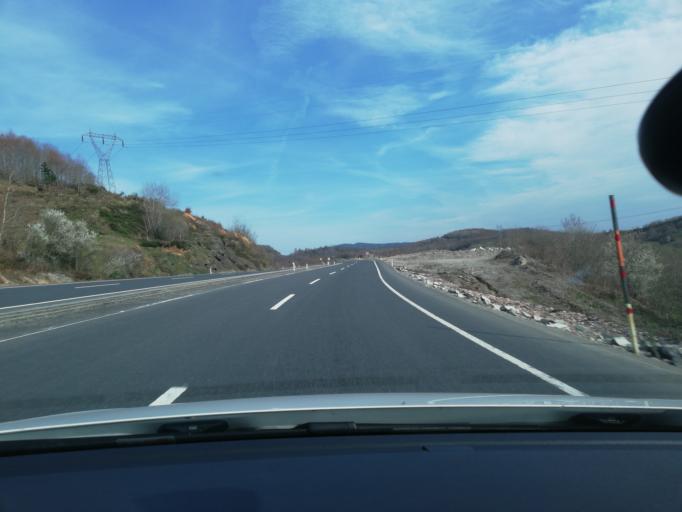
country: TR
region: Zonguldak
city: Eregli
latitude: 41.3311
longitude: 31.5806
